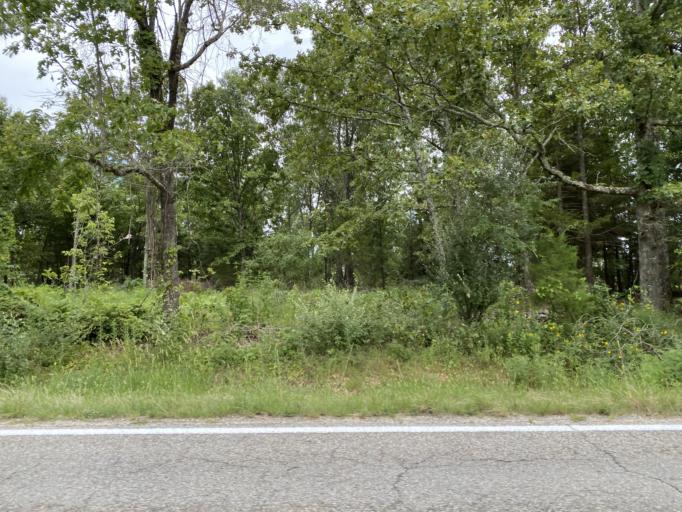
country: US
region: Arkansas
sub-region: Fulton County
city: Salem
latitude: 36.4184
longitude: -91.7185
